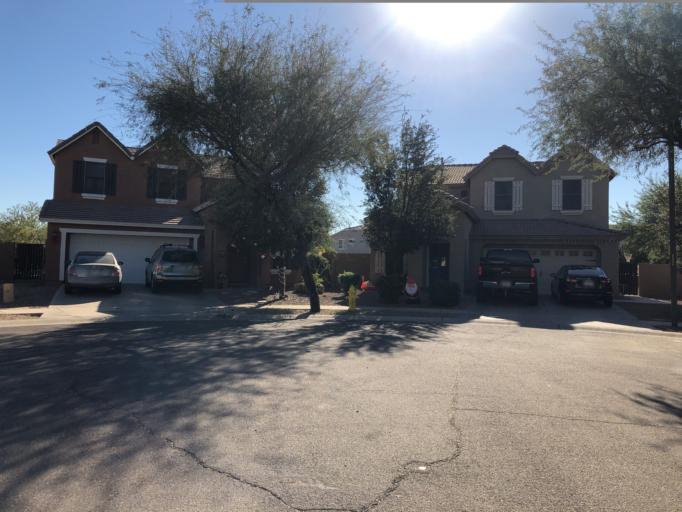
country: US
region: Arizona
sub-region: Maricopa County
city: Queen Creek
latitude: 33.2712
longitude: -111.7040
